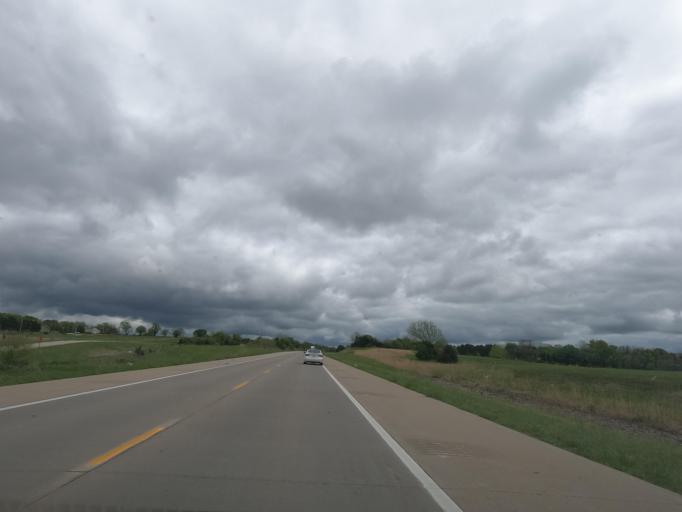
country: US
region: Kansas
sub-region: Wilson County
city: Neodesha
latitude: 37.3550
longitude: -95.6413
